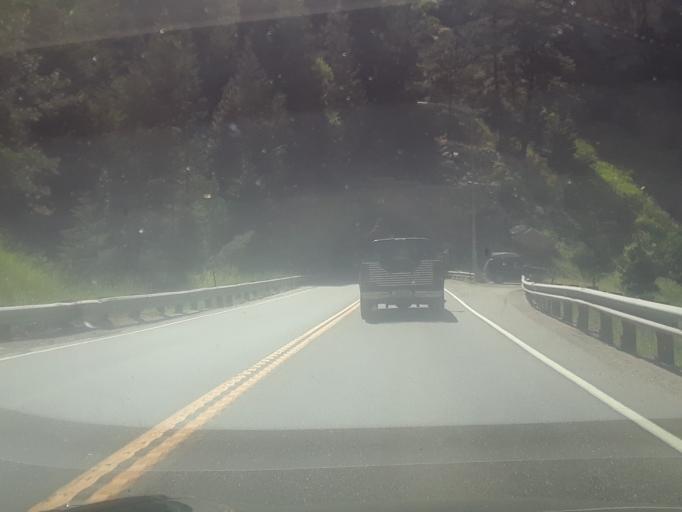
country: US
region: Colorado
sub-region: Clear Creek County
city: Idaho Springs
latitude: 39.7404
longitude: -105.4109
